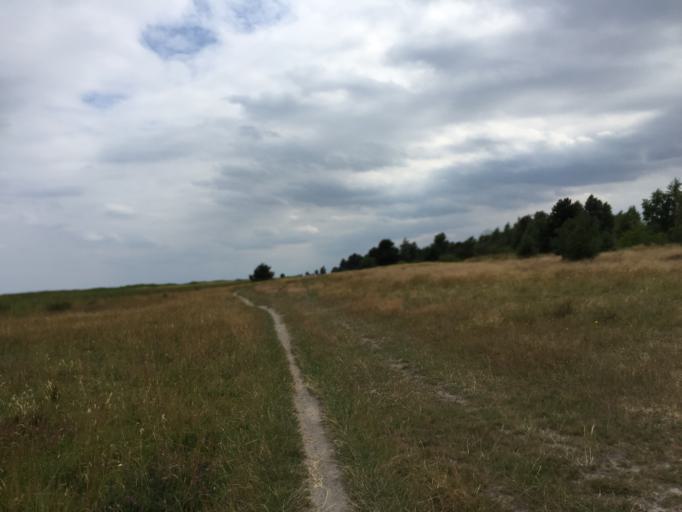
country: DE
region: Mecklenburg-Vorpommern
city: Hiddensee
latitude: 54.4995
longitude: 13.0721
